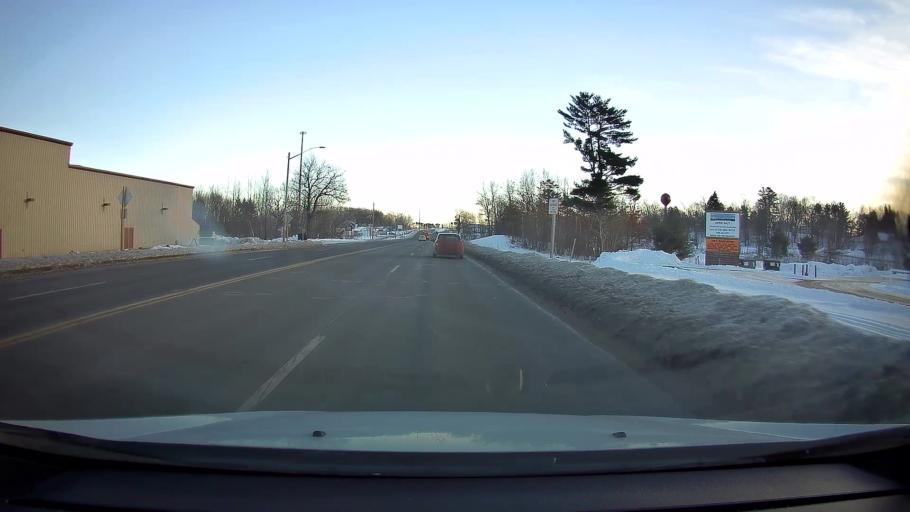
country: US
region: Wisconsin
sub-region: Barron County
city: Turtle Lake
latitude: 45.3968
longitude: -92.1491
